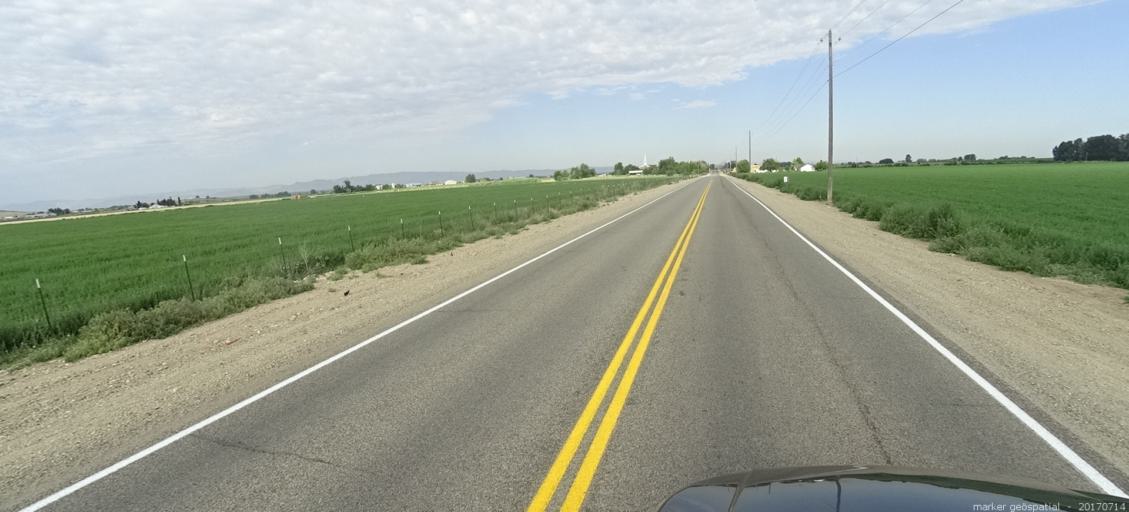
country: US
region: Idaho
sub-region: Ada County
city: Kuna
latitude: 43.4884
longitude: -116.4462
